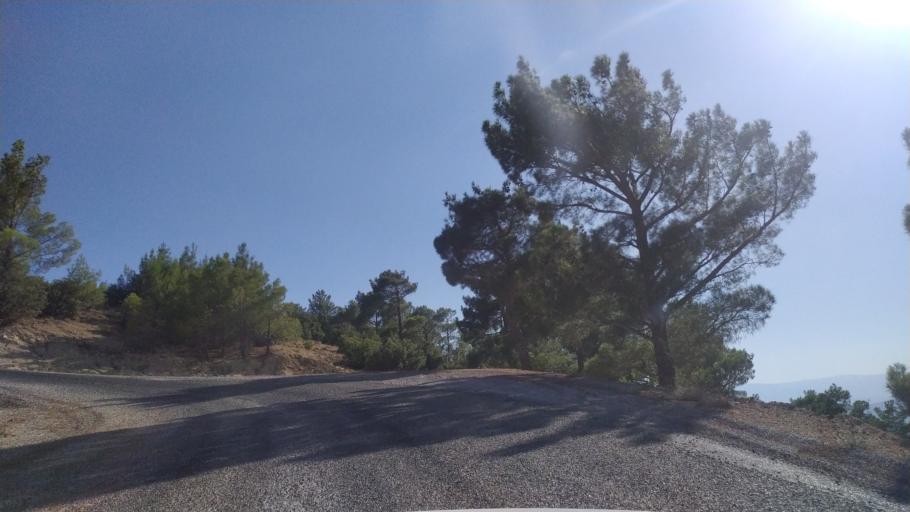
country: TR
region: Mersin
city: Mut
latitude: 36.7026
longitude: 33.4743
